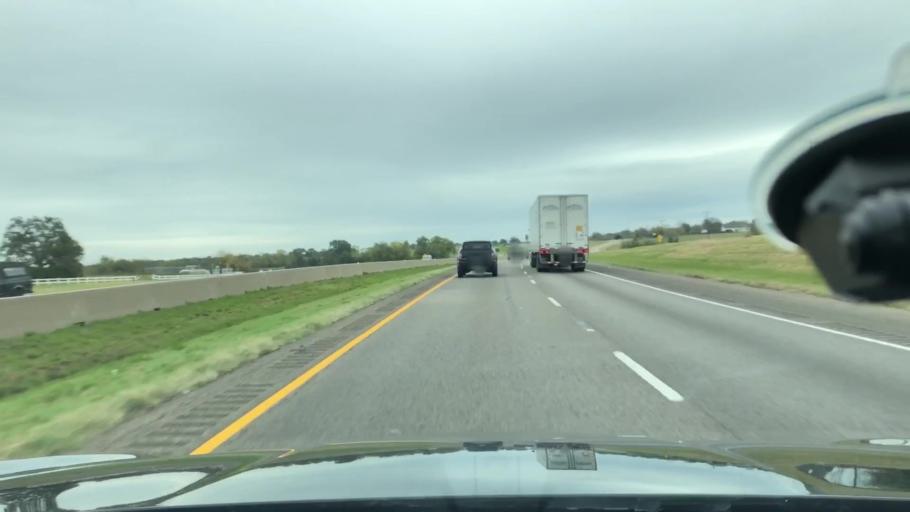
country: US
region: Texas
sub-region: Hopkins County
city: Sulphur Springs
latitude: 33.1481
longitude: -95.5326
